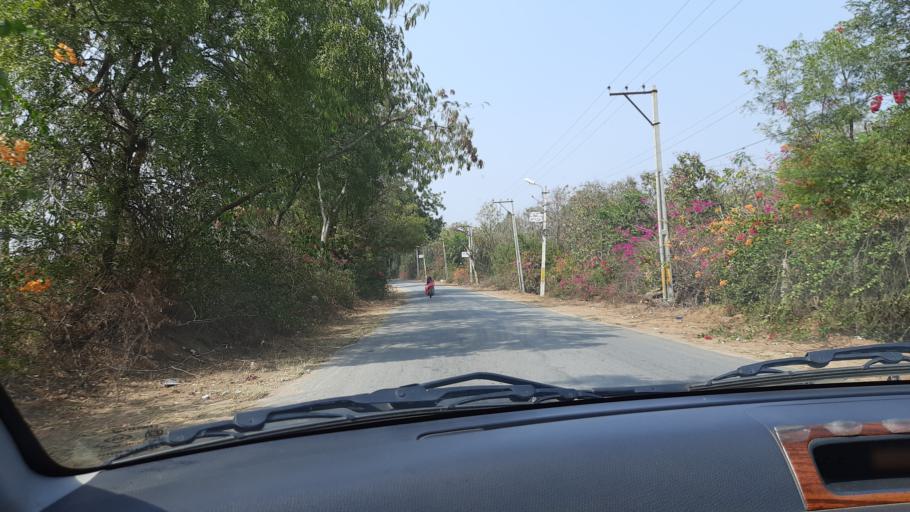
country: IN
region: Telangana
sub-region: Rangareddi
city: Lal Bahadur Nagar
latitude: 17.2788
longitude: 78.6541
